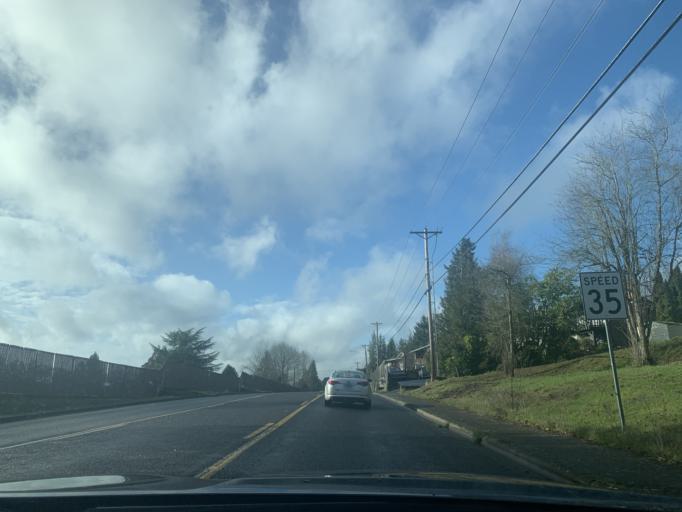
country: US
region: Oregon
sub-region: Washington County
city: King City
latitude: 45.4106
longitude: -122.7982
